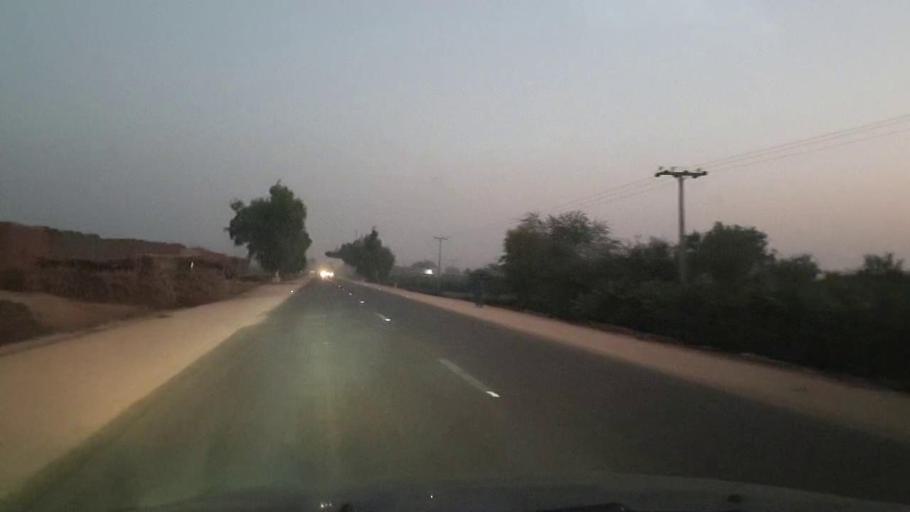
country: PK
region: Sindh
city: Tando Allahyar
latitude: 25.4016
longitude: 68.7623
